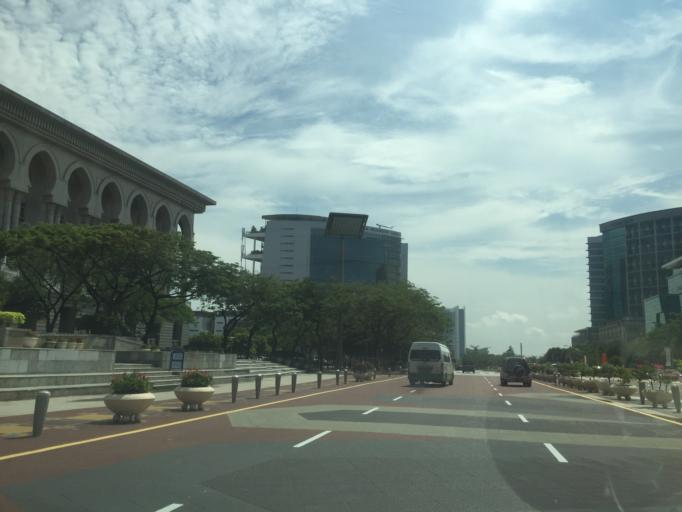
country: MY
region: Putrajaya
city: Putrajaya
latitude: 2.9177
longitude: 101.6853
